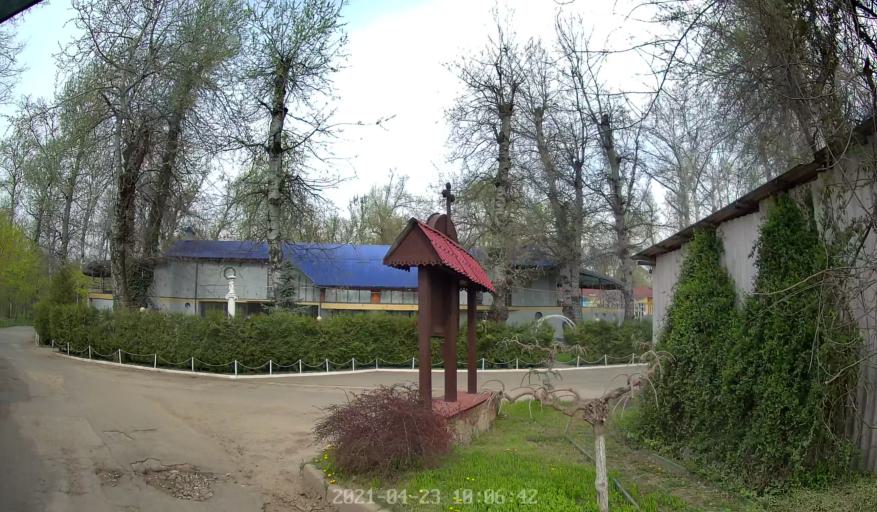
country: MD
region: Chisinau
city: Vadul lui Voda
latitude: 47.0847
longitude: 29.1123
